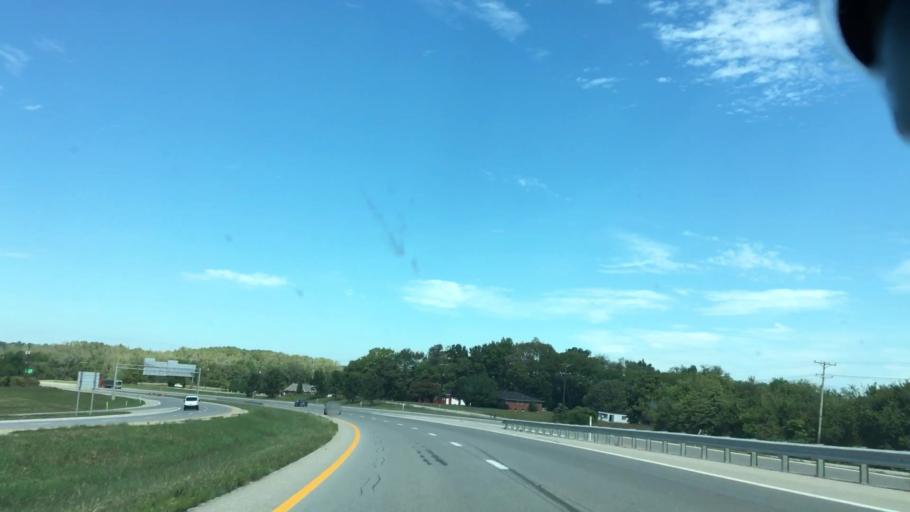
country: US
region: Kentucky
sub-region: Christian County
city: Hopkinsville
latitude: 36.8470
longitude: -87.4616
